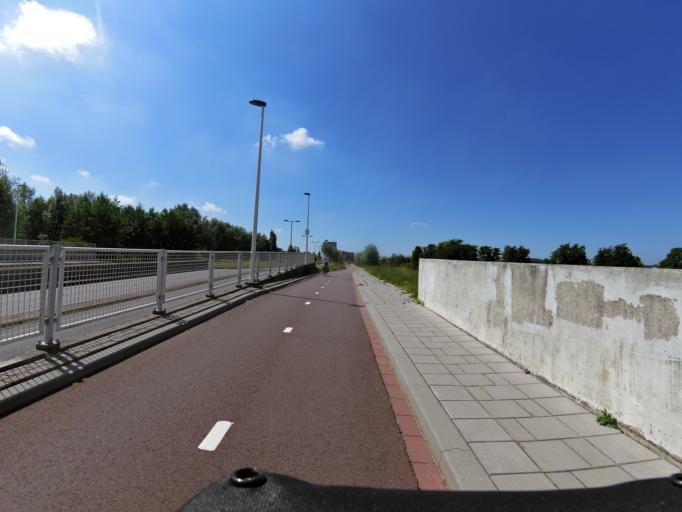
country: NL
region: South Holland
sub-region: Gemeente Schiedam
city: Schiedam
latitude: 51.9382
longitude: 4.3925
